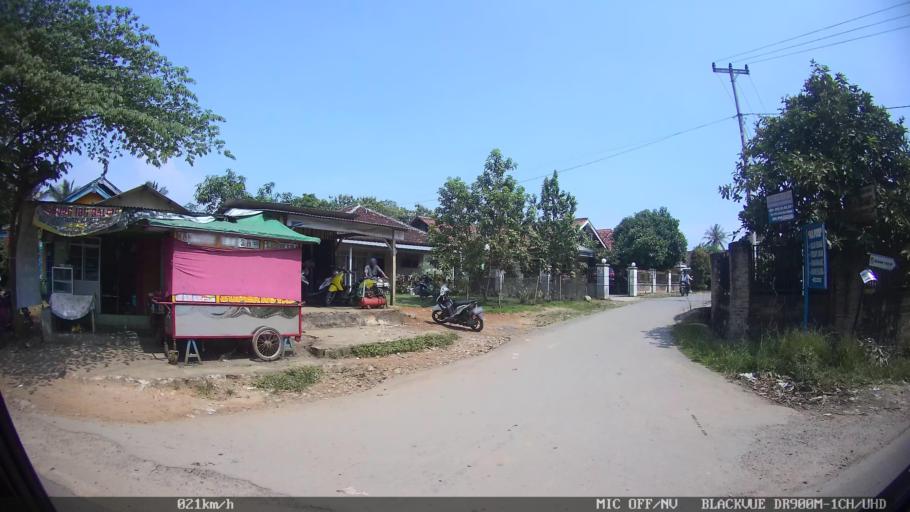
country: ID
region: Lampung
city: Natar
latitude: -5.3094
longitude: 105.2115
